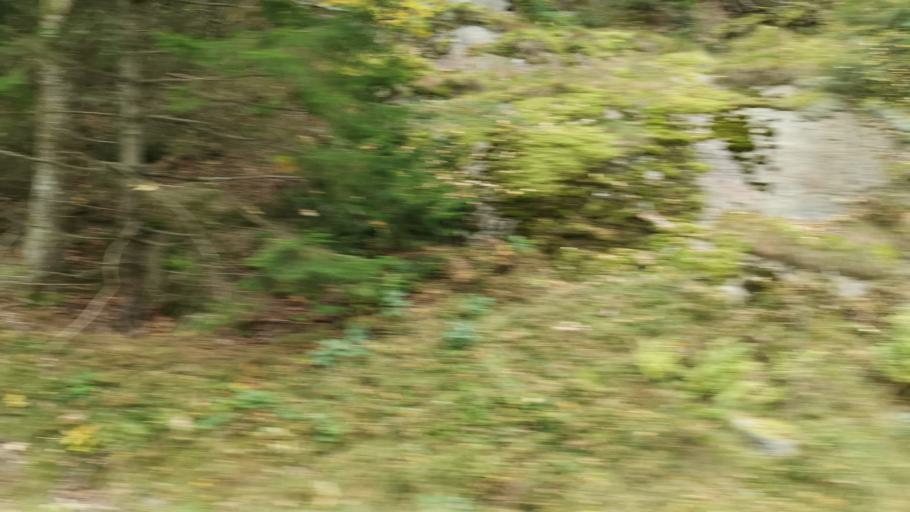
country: SE
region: Vaestra Goetaland
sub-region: Tanums Kommun
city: Tanumshede
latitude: 58.5873
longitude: 11.3621
